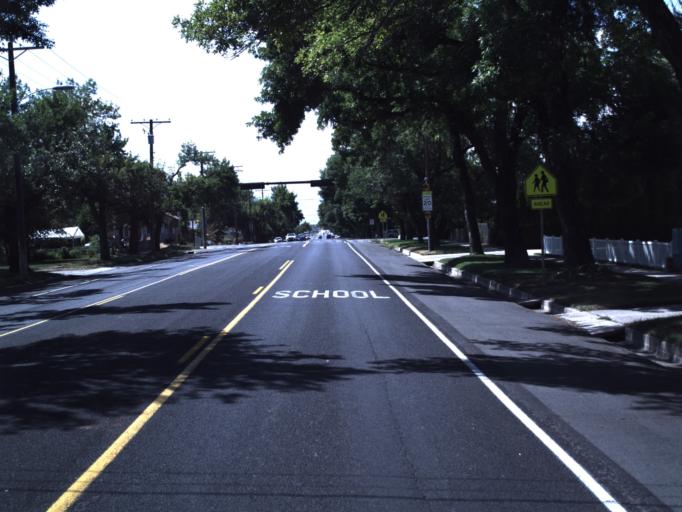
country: US
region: Utah
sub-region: Cache County
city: Logan
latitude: 41.7354
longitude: -111.8438
